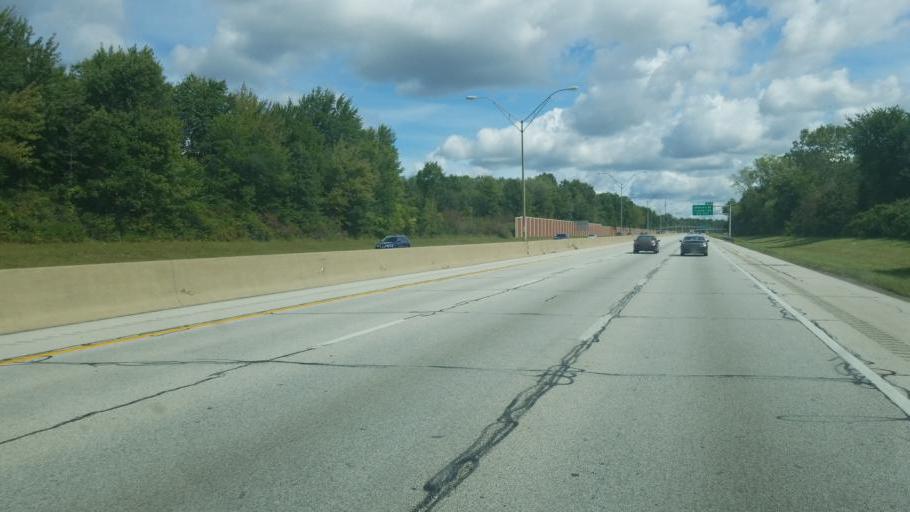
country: US
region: Ohio
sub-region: Cuyahoga County
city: North Olmsted
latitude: 41.3913
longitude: -81.9552
